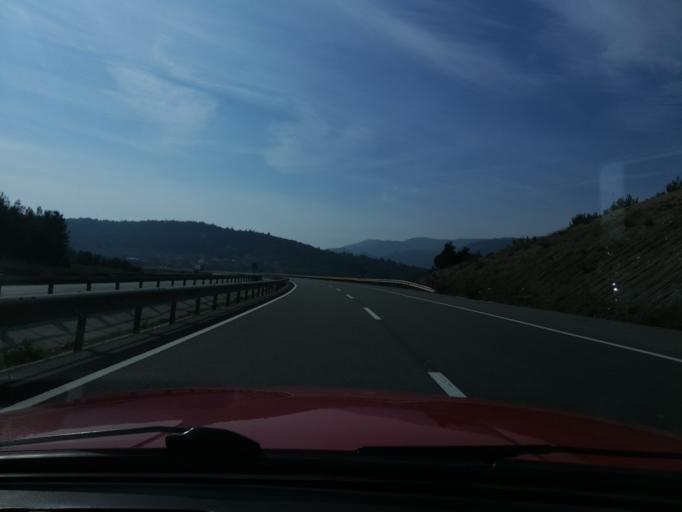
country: TR
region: Bilecik
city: Osmaneli
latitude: 40.3837
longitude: 29.9960
